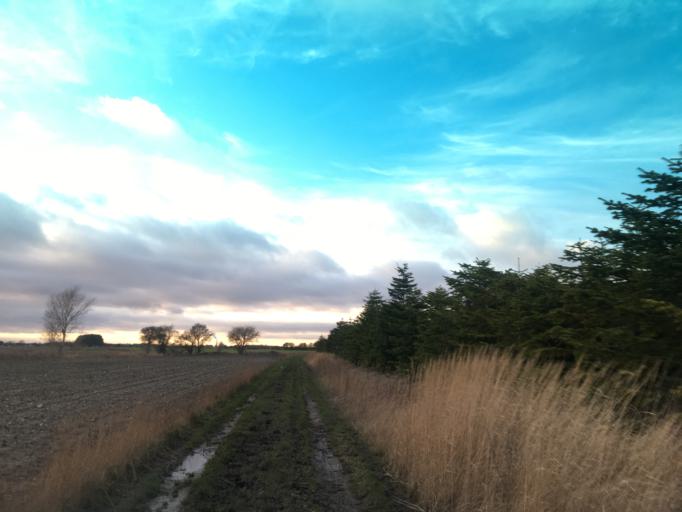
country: DK
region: Capital Region
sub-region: Dragor Kommune
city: Dragor
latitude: 55.5846
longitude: 12.6201
